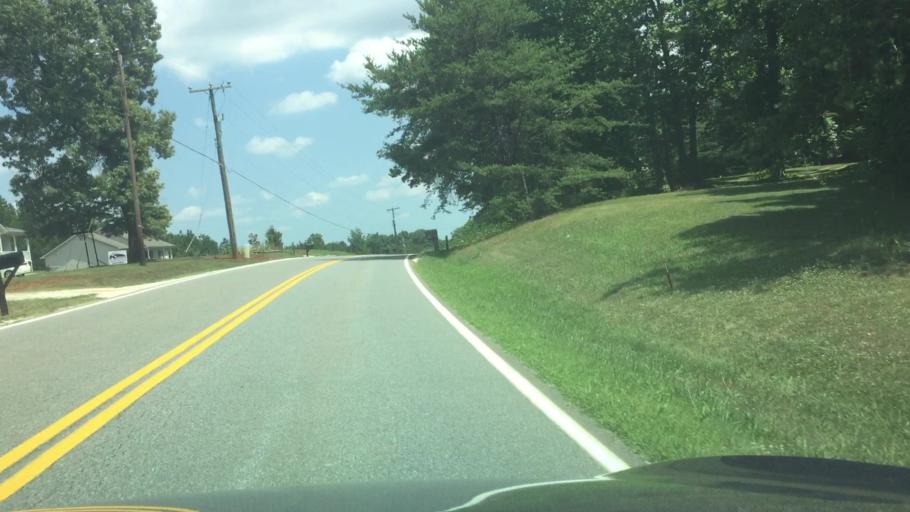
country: US
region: Virginia
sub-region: Campbell County
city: Concord
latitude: 37.3444
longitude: -78.9038
